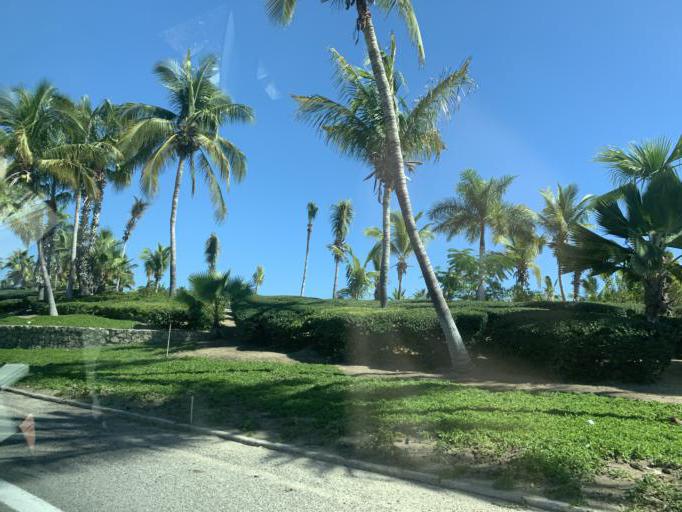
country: MX
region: Baja California Sur
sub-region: Los Cabos
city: San Jose del Cabo
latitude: 23.0136
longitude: -109.7229
